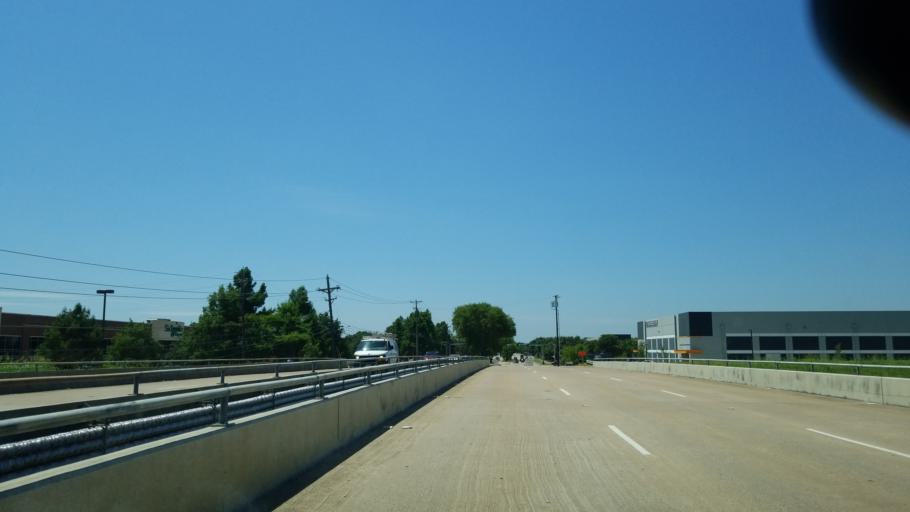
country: US
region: Texas
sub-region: Dallas County
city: Carrollton
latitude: 32.9473
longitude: -96.9251
